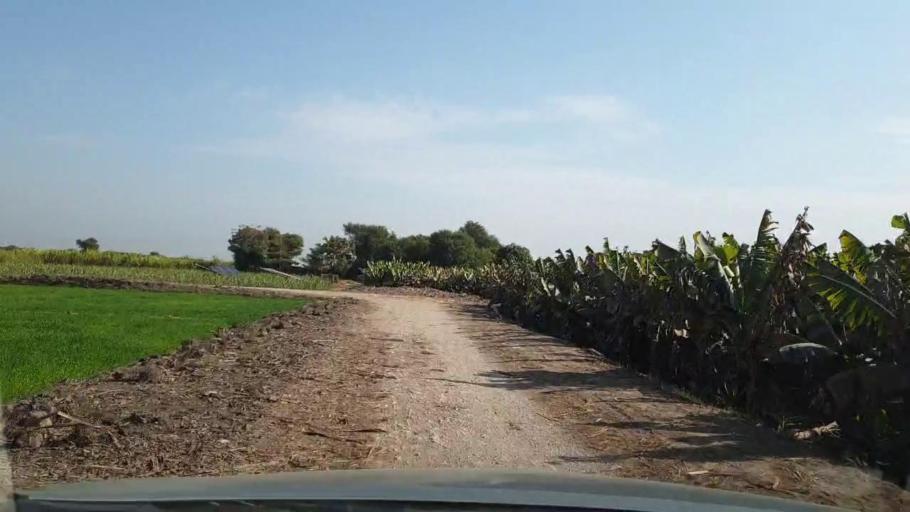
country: PK
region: Sindh
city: Tando Allahyar
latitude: 25.5773
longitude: 68.6105
